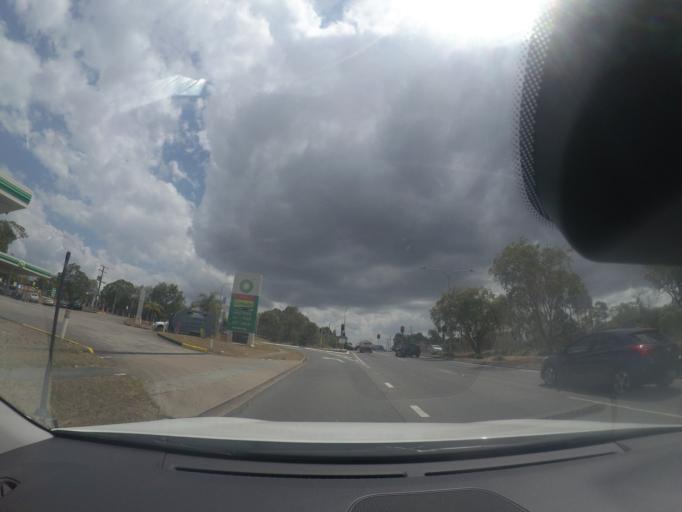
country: AU
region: Queensland
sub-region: Logan
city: Woodridge
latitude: -27.6174
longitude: 153.0941
